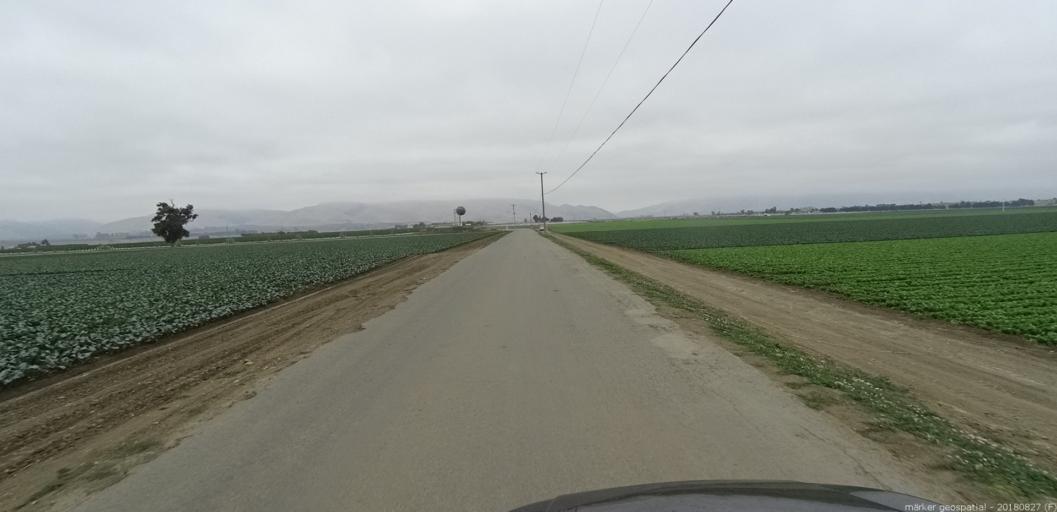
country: US
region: California
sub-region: Monterey County
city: Greenfield
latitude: 36.3151
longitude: -121.2178
